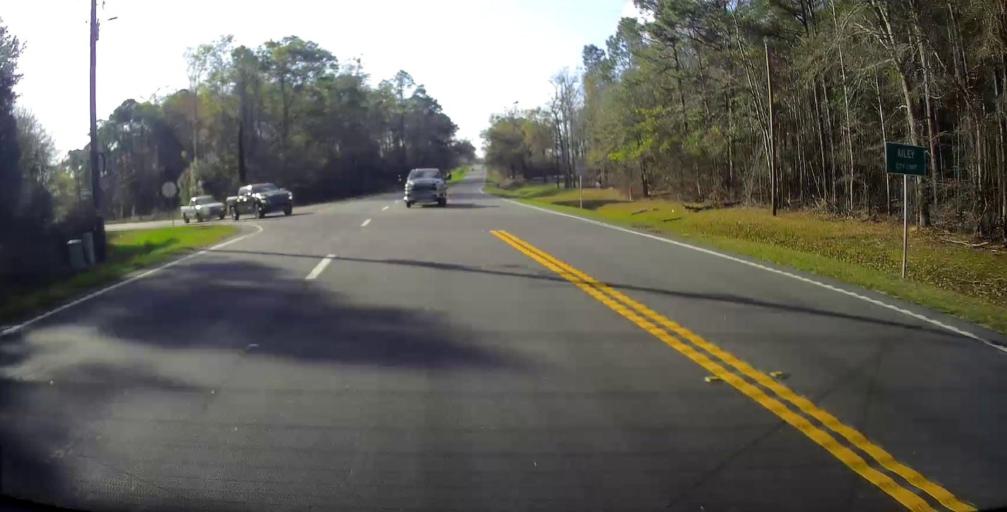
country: US
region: Georgia
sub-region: Montgomery County
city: Mount Vernon
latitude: 32.1802
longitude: -82.5560
